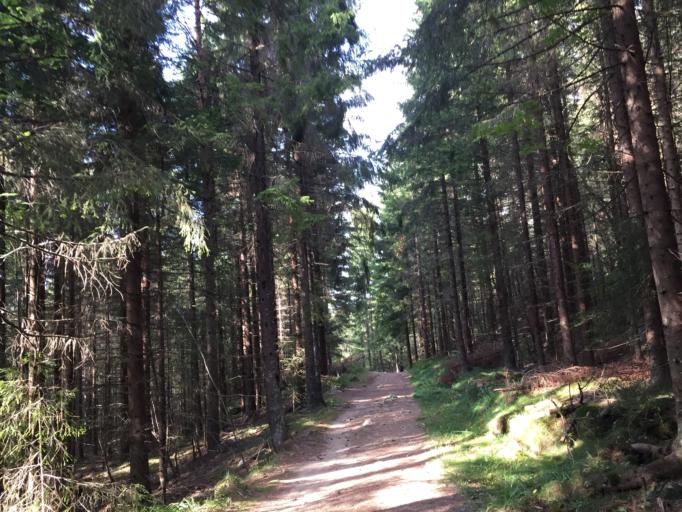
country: NO
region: Akershus
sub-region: Raelingen
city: Fjerdingby
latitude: 59.9169
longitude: 11.0283
